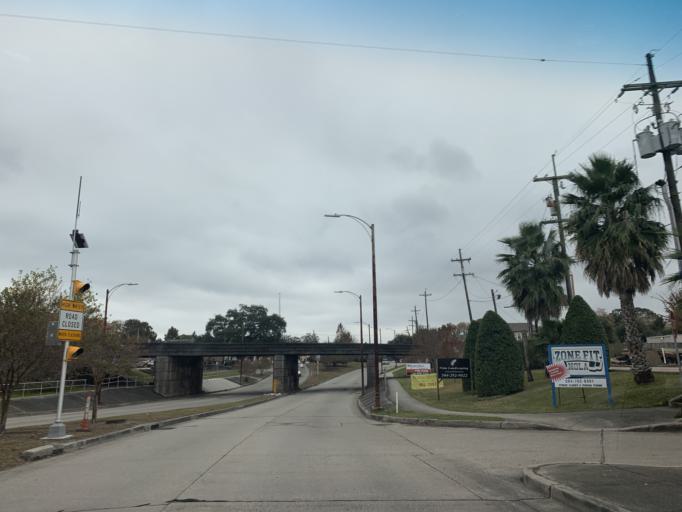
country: US
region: Louisiana
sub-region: Jefferson Parish
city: Metairie
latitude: 29.9919
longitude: -90.1097
